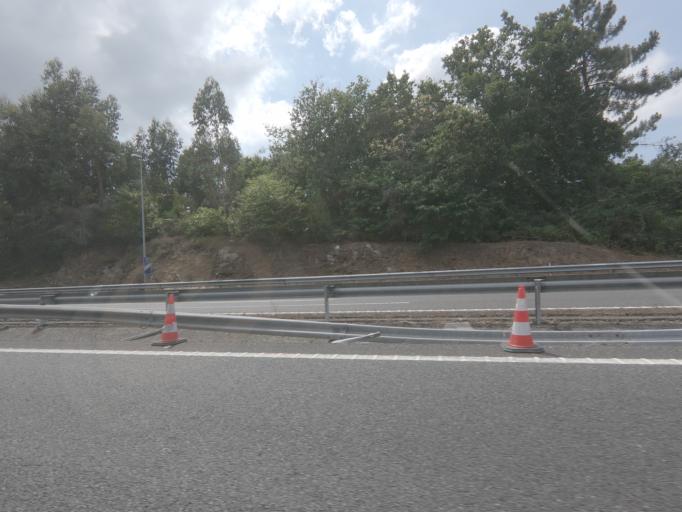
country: ES
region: Galicia
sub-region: Provincia de Pontevedra
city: Tui
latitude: 42.0541
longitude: -8.6550
